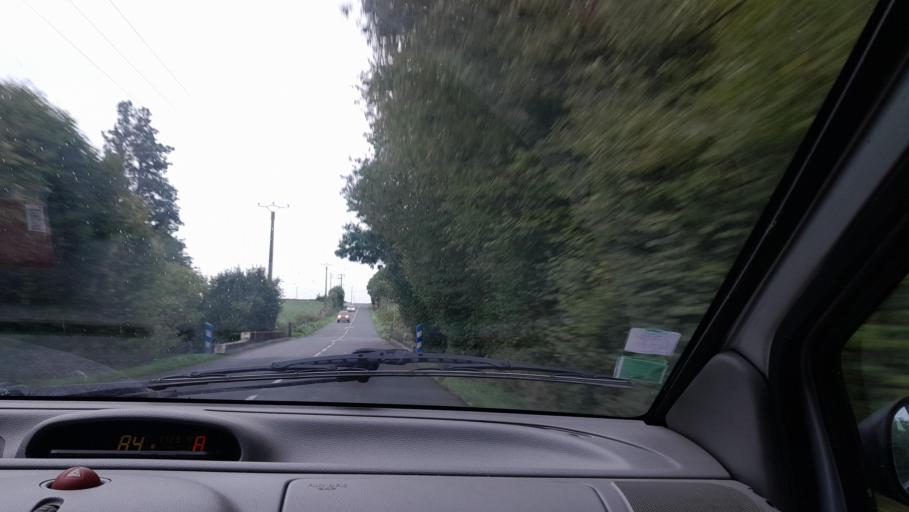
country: FR
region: Pays de la Loire
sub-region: Departement de Maine-et-Loire
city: Pouance
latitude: 47.7224
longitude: -1.1778
